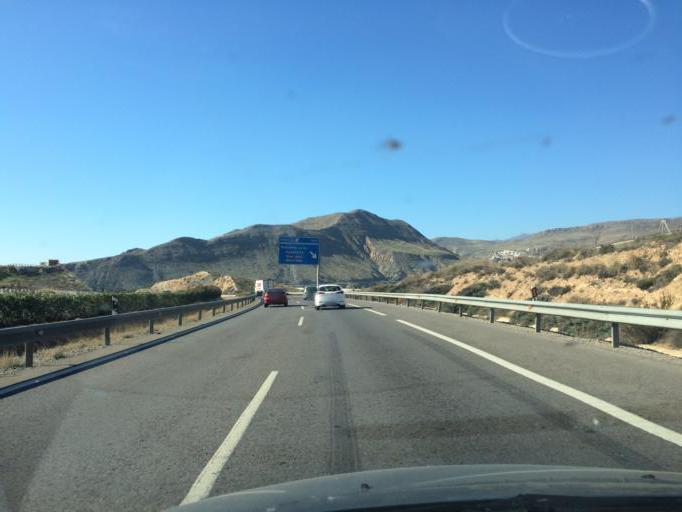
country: ES
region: Andalusia
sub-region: Provincia de Almeria
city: Aguadulce
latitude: 36.8276
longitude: -2.5867
